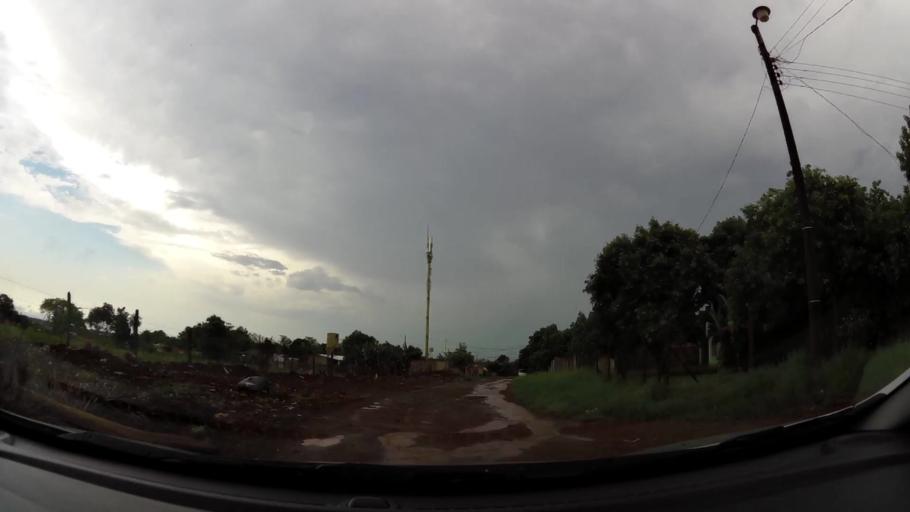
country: PY
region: Alto Parana
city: Presidente Franco
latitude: -25.5450
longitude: -54.6489
